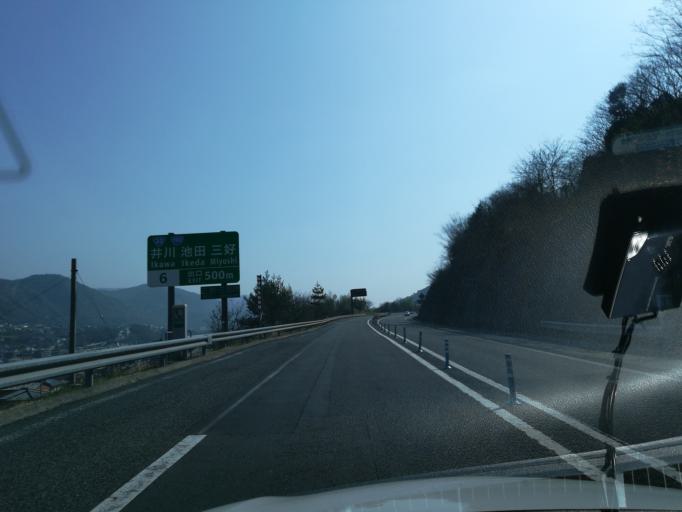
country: JP
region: Tokushima
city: Ikedacho
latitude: 34.0287
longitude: 133.8322
